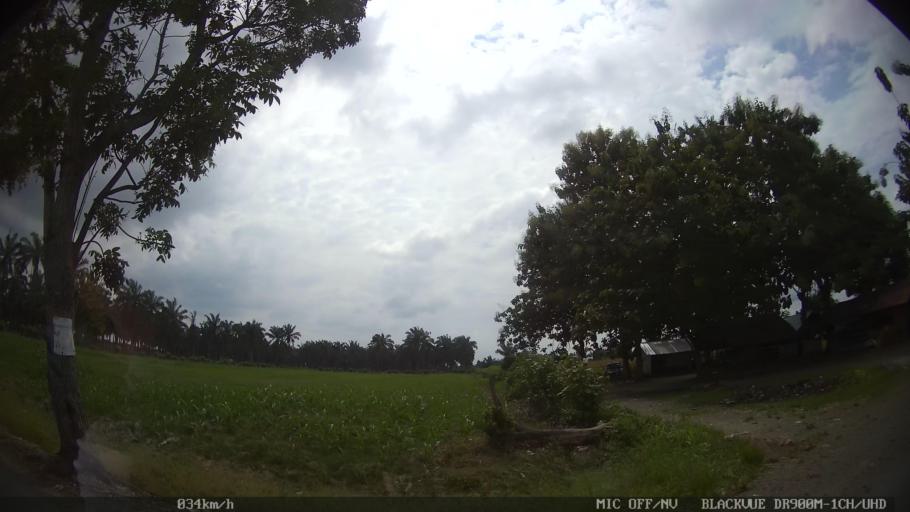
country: ID
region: North Sumatra
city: Sunggal
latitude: 3.6302
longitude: 98.6062
